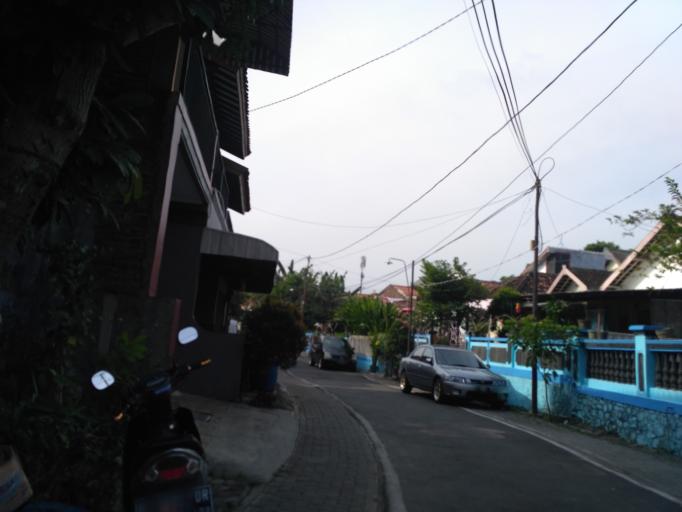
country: ID
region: Central Java
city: Semarang
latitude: -7.0124
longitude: 110.4435
